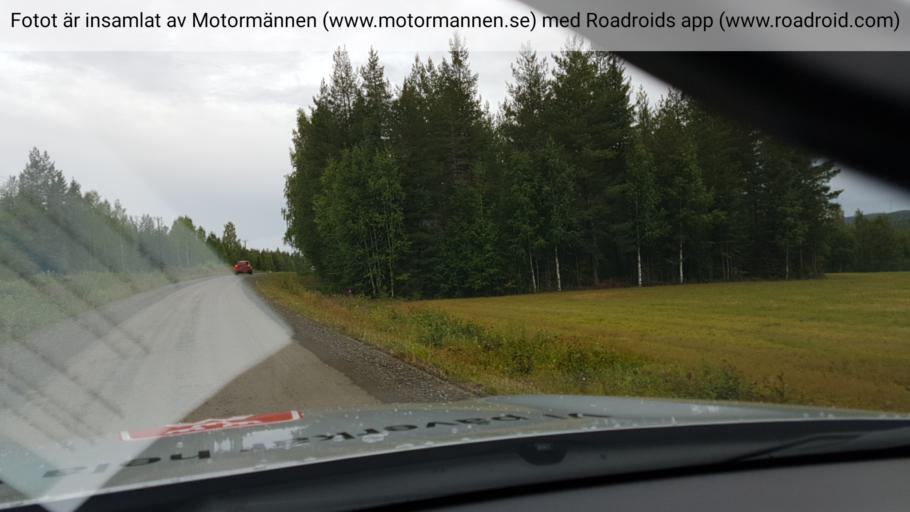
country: SE
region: Norrbotten
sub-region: Alvsbyns Kommun
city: AElvsbyn
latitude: 65.9905
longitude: 21.1935
